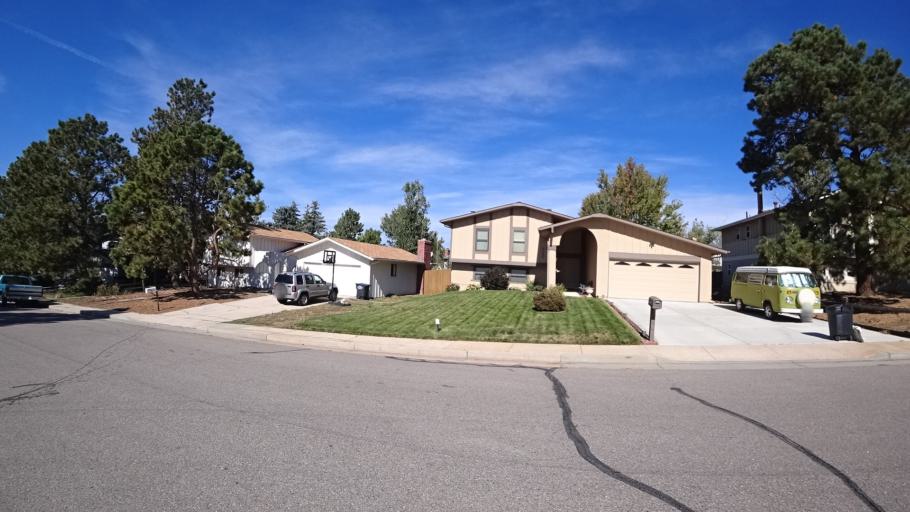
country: US
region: Colorado
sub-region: El Paso County
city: Cimarron Hills
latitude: 38.9156
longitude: -104.7699
